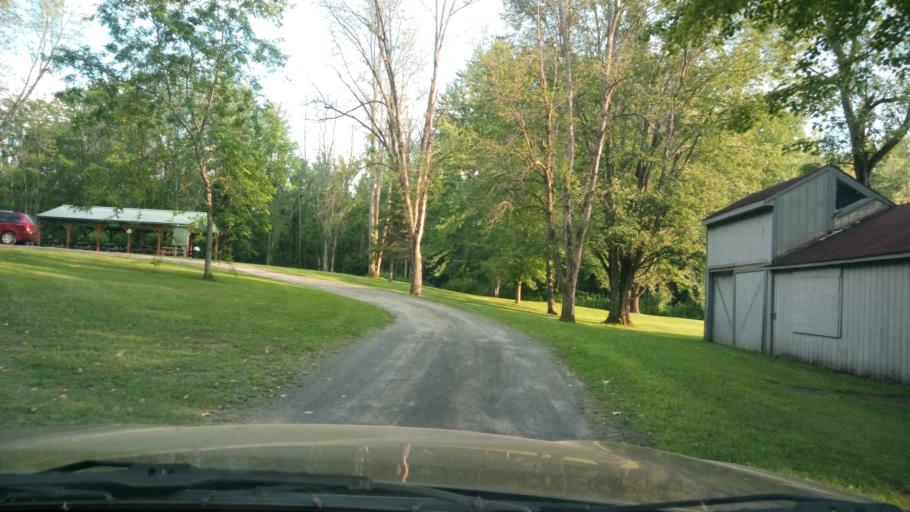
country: US
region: New York
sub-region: Wayne County
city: Lyons
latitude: 43.0795
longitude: -76.9332
